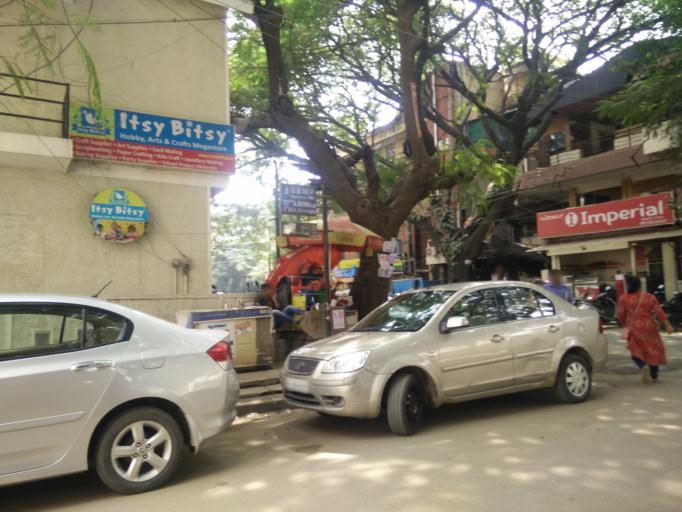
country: IN
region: Karnataka
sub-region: Bangalore Urban
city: Bangalore
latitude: 12.9366
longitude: 77.6252
